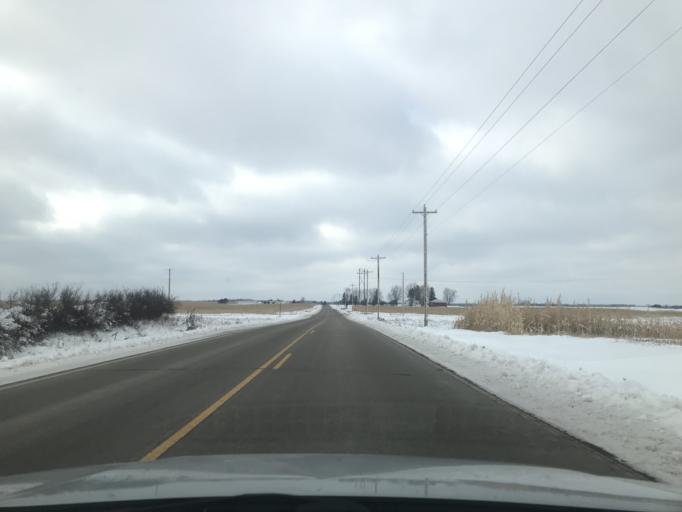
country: US
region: Wisconsin
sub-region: Oconto County
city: Oconto
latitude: 44.9498
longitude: -87.9247
